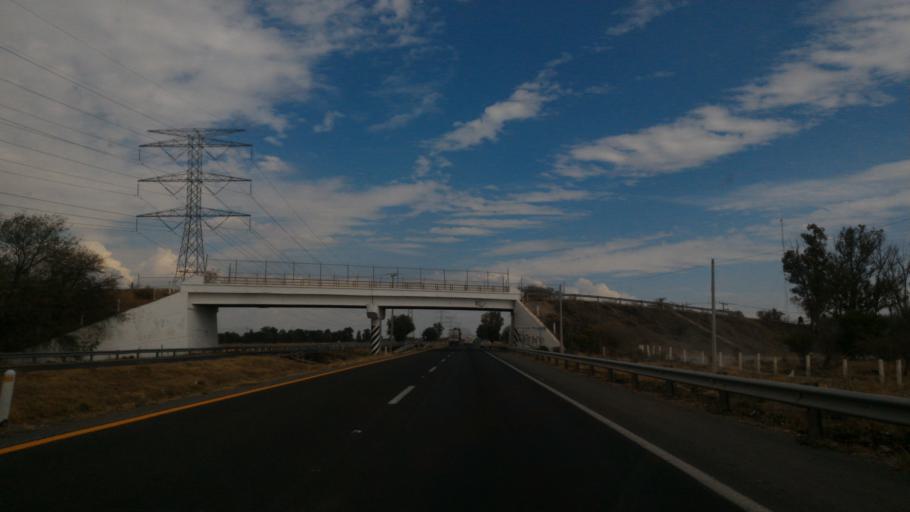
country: MX
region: Guanajuato
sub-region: Leon
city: San Jose de Duran (Los Troncoso)
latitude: 21.0609
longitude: -101.6601
